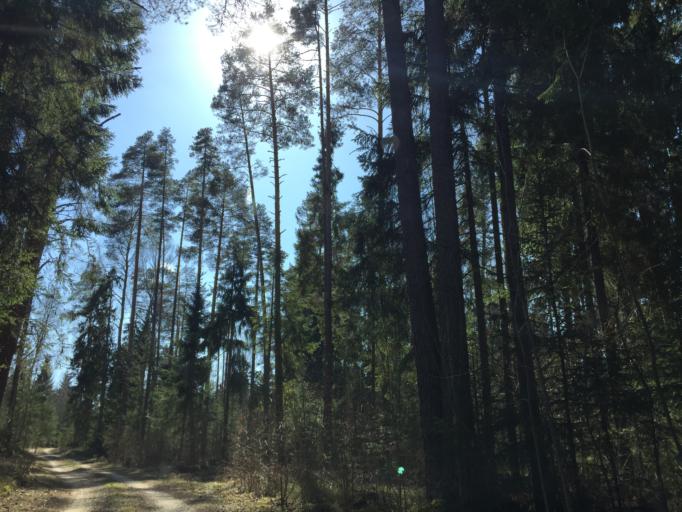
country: EE
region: Viljandimaa
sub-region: Viljandi linn
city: Viljandi
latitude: 58.2715
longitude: 25.6037
